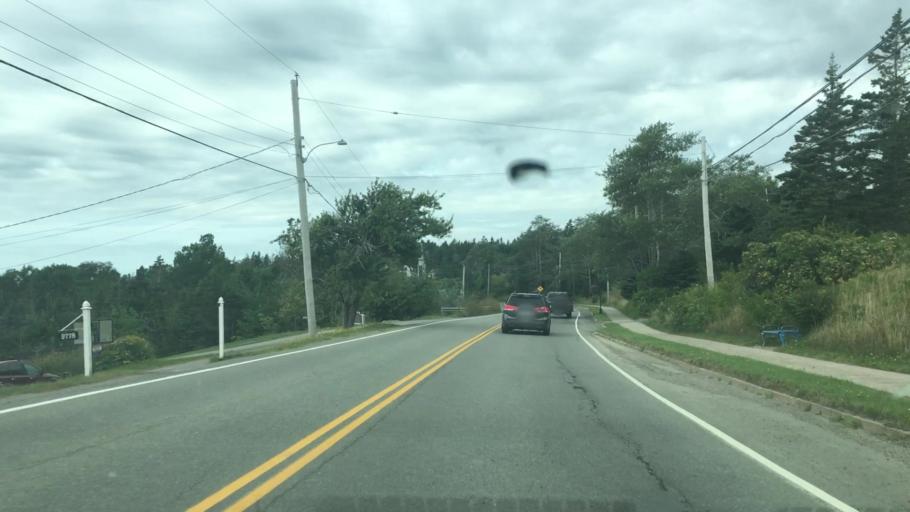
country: CA
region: Nova Scotia
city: Princeville
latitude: 45.6556
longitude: -60.8849
